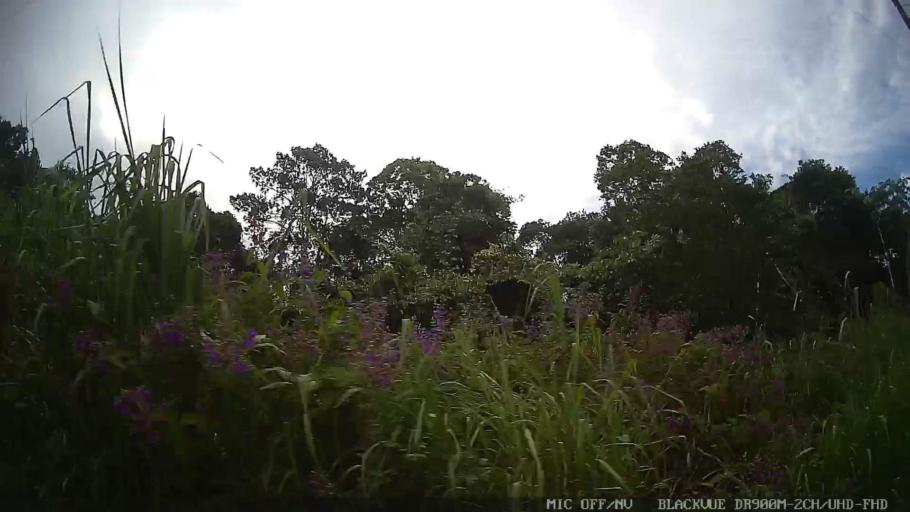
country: BR
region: Sao Paulo
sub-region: Iguape
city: Iguape
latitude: -24.6537
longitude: -47.4046
